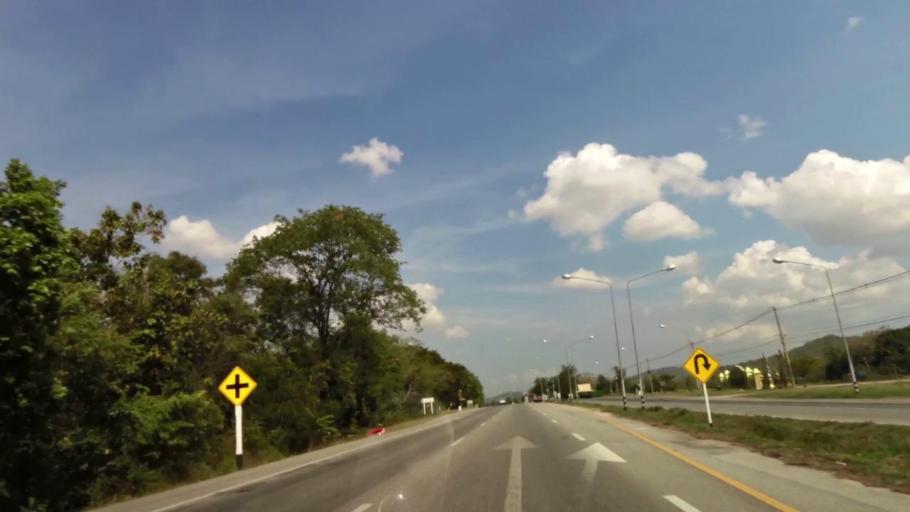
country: TH
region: Uttaradit
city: Thong Saen Khan
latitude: 17.4509
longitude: 100.2363
